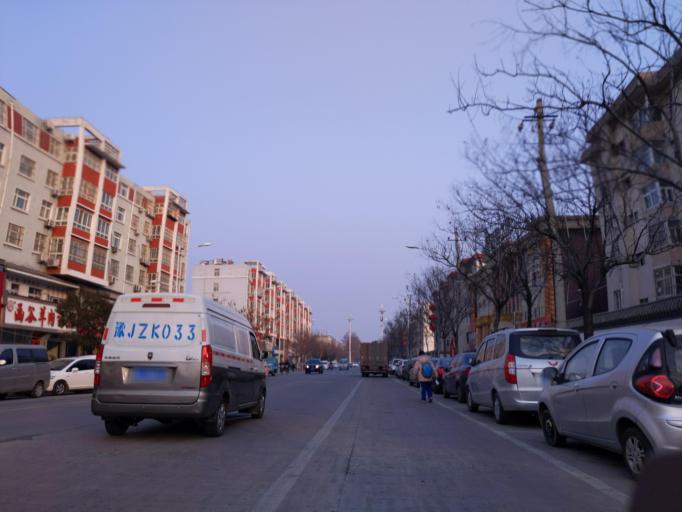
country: CN
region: Henan Sheng
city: Zhongyuanlu
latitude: 35.7825
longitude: 115.0585
